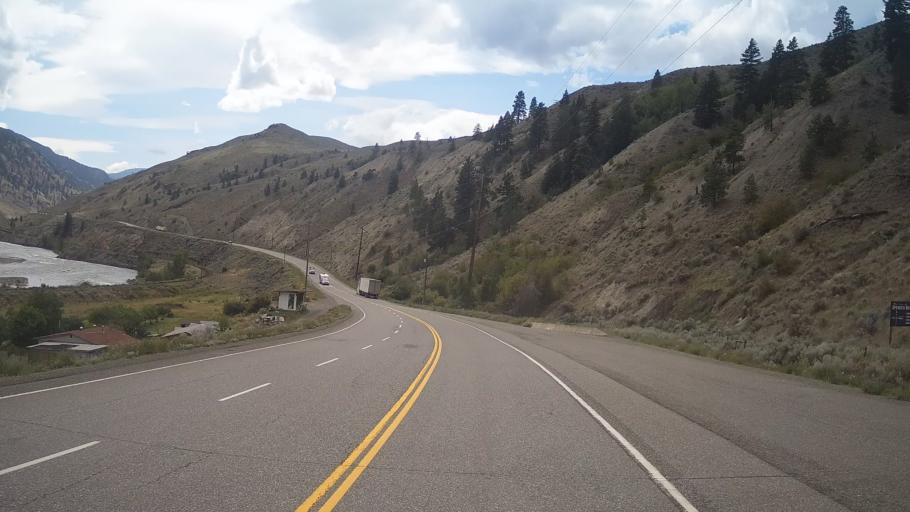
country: CA
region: British Columbia
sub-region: Thompson-Nicola Regional District
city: Ashcroft
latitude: 50.4844
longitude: -121.3012
